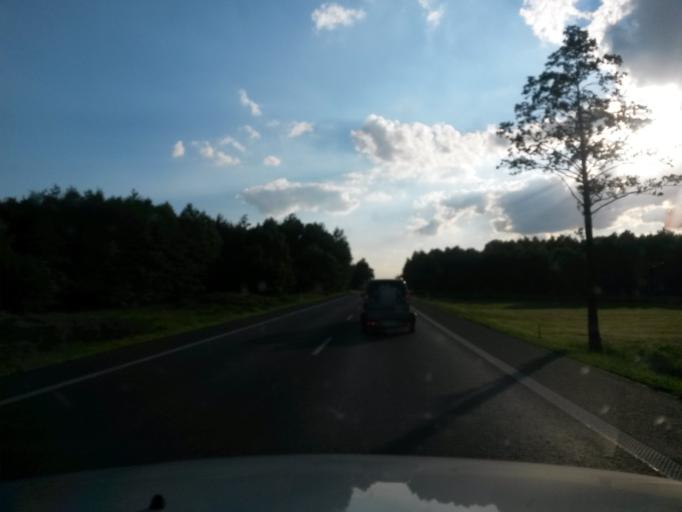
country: PL
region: Lodz Voivodeship
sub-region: Powiat belchatowski
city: Rusiec
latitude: 51.3137
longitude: 18.9183
